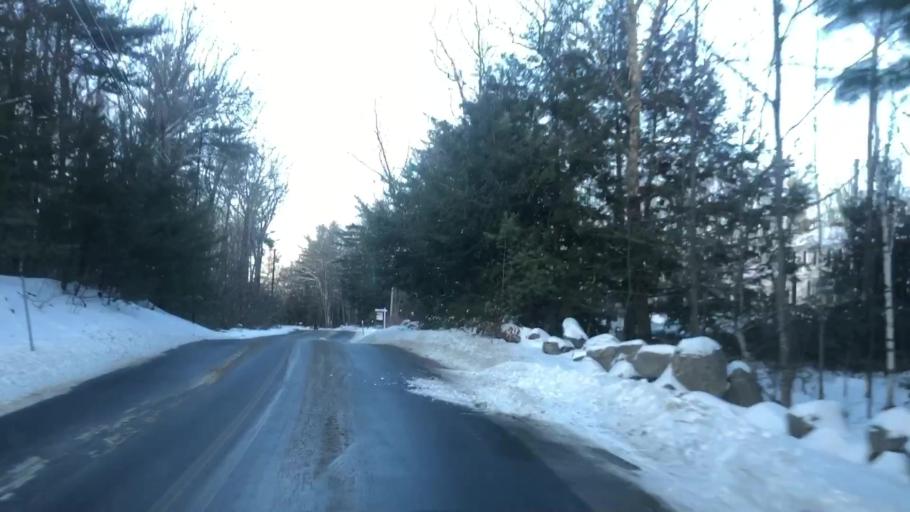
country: US
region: New Hampshire
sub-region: Hillsborough County
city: Milford
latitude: 42.8029
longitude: -71.6697
